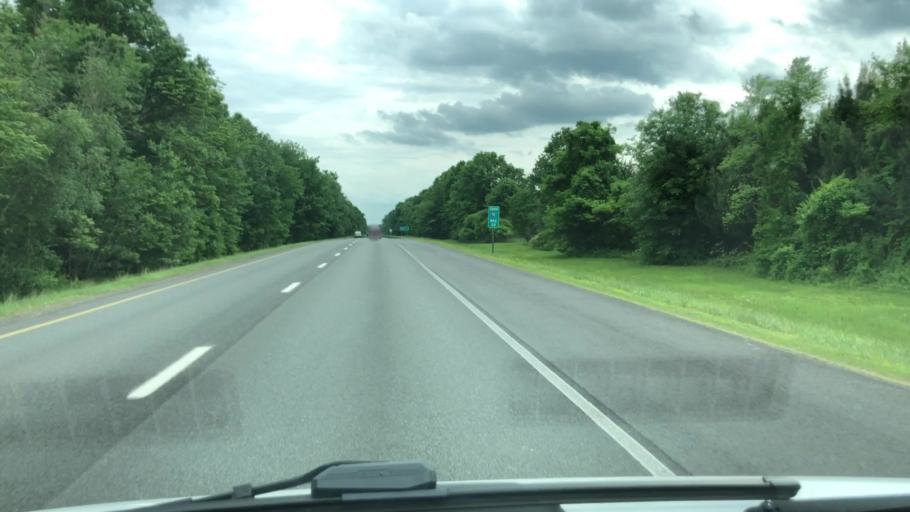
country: US
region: Massachusetts
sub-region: Franklin County
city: Whately
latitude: 42.4284
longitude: -72.6231
